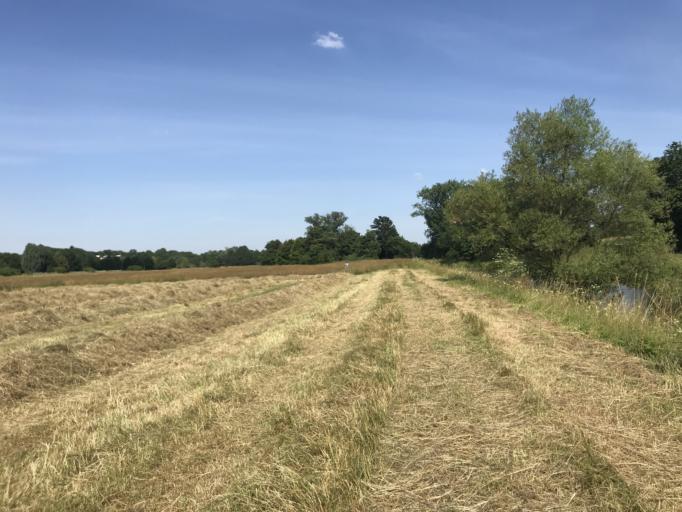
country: DE
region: Hesse
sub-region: Regierungsbezirk Darmstadt
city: Bad Homburg vor der Hoehe
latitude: 50.1752
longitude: 8.6568
